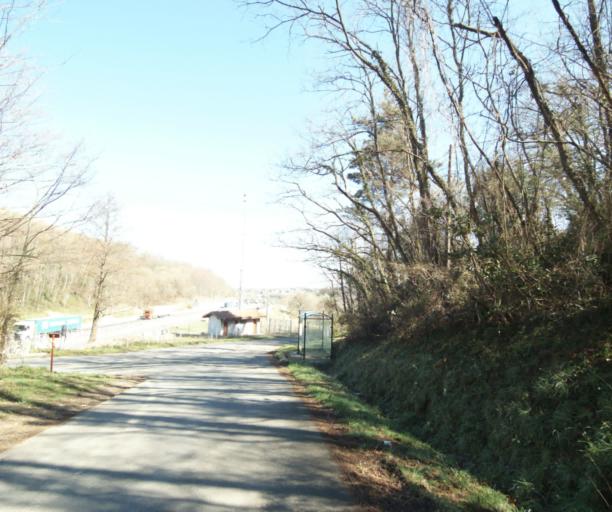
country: FR
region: Aquitaine
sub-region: Departement des Pyrenees-Atlantiques
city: Urrugne
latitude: 43.3413
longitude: -1.7282
